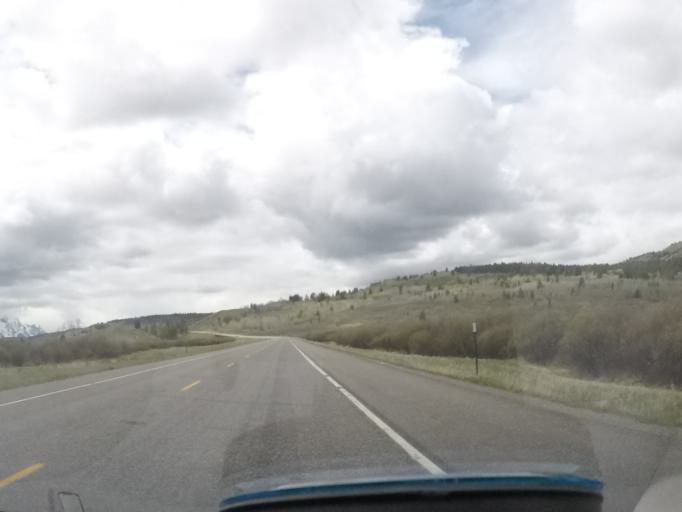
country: US
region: Wyoming
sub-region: Teton County
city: Jackson
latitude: 43.8354
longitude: -110.4317
